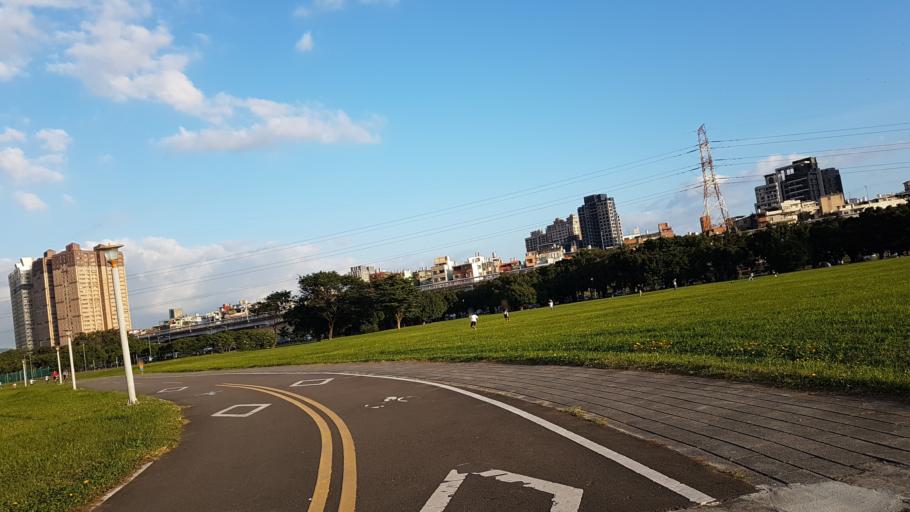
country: TW
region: Taipei
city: Taipei
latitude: 25.0185
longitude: 121.5061
